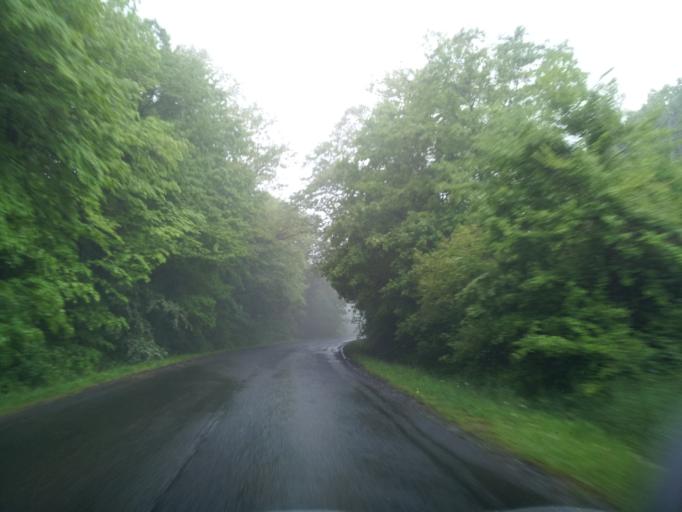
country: HU
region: Baranya
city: Hosszuheteny
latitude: 46.1707
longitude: 18.3300
